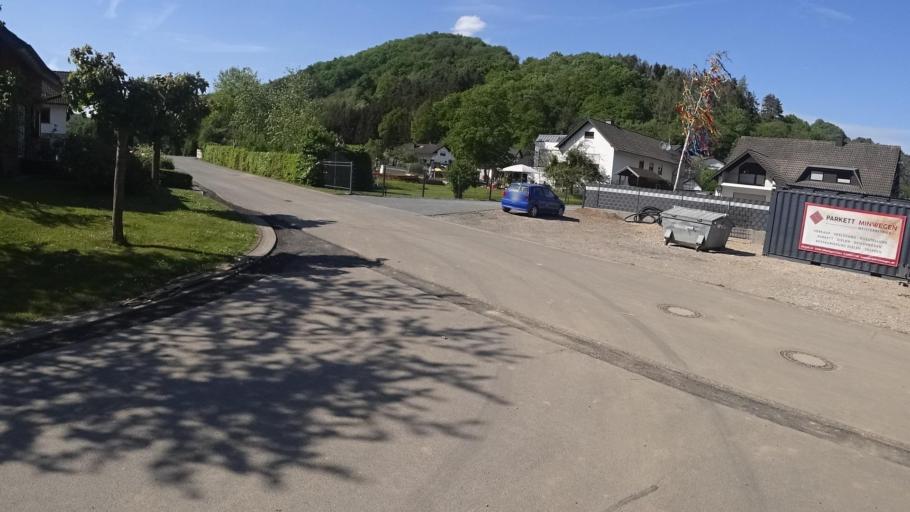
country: DE
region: Rheinland-Pfalz
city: Honningen
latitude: 50.4576
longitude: 6.9427
